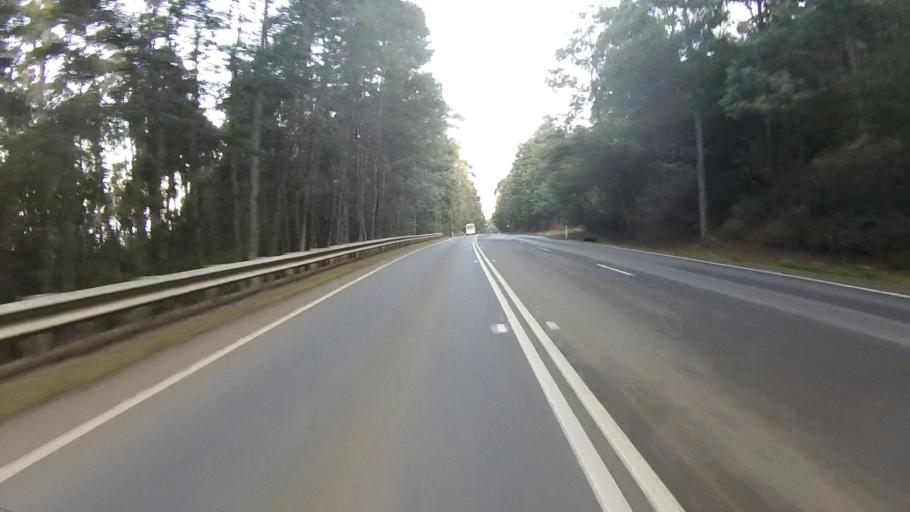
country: AU
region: Tasmania
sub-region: Sorell
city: Sorell
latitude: -43.0063
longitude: 147.9267
